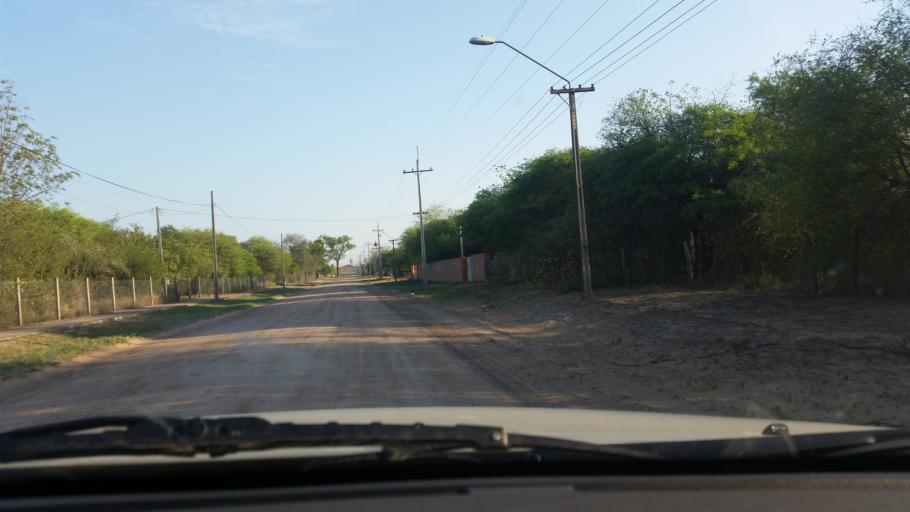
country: PY
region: Boqueron
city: Filadelfia
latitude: -22.3448
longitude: -60.0388
